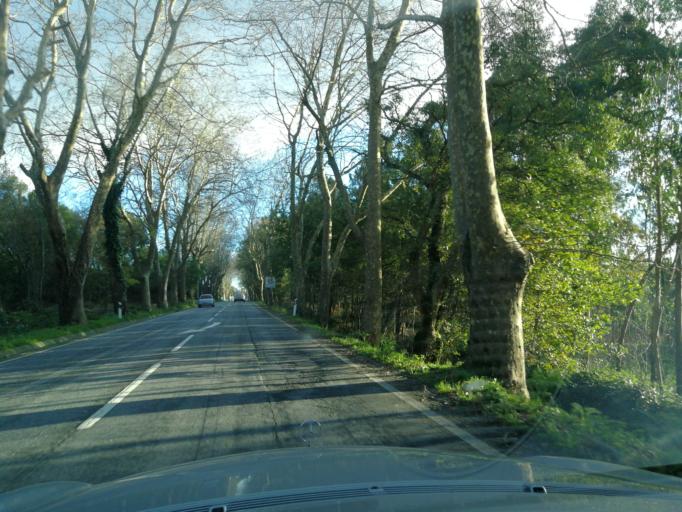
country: PT
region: Viana do Castelo
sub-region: Viana do Castelo
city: Darque
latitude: 41.6264
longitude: -8.7590
